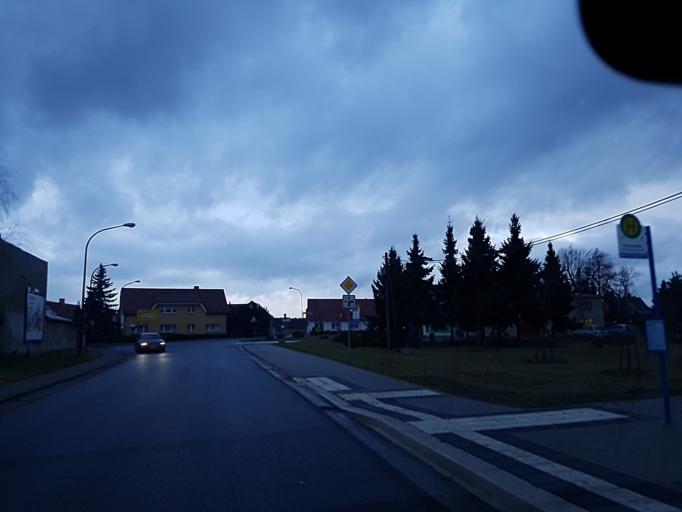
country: DE
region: Brandenburg
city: Finsterwalde
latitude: 51.5681
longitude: 13.6722
